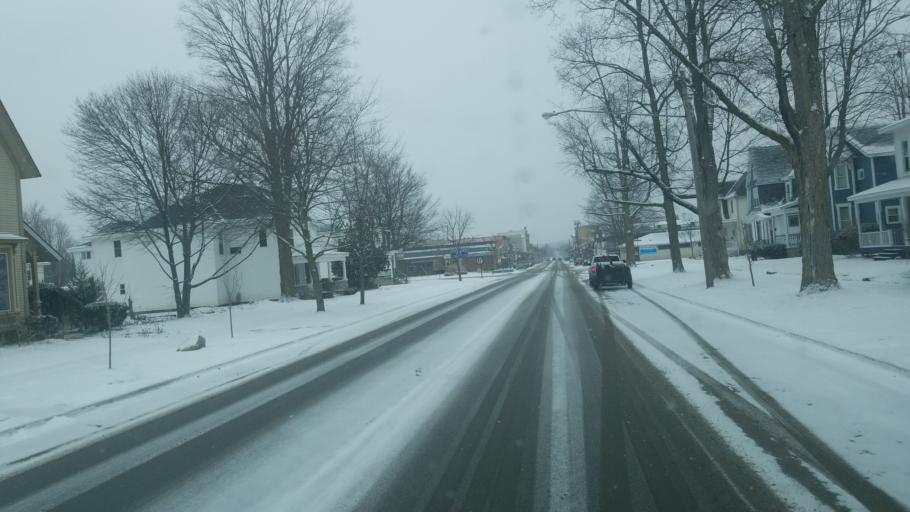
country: US
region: Michigan
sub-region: Mecosta County
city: Big Rapids
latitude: 43.6947
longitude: -85.4819
